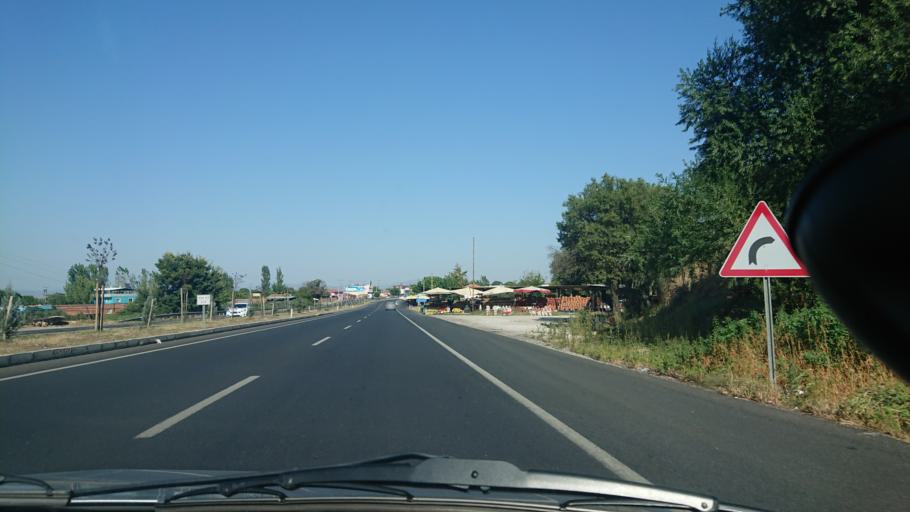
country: TR
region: Manisa
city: Ahmetli
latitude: 38.4880
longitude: 27.8342
